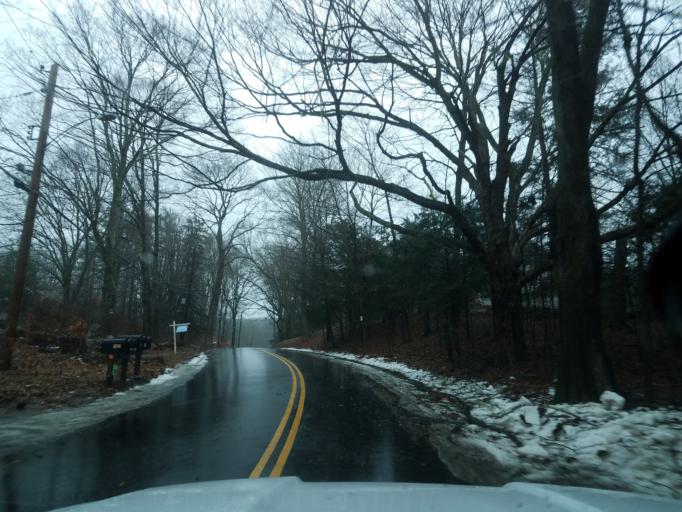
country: US
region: Connecticut
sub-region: New Haven County
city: Hamden
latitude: 41.4041
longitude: -72.8920
